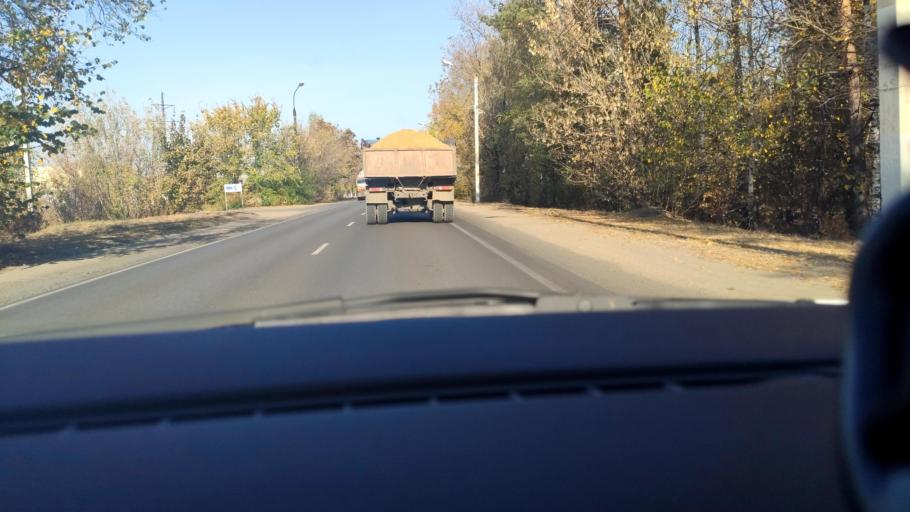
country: RU
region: Voronezj
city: Pridonskoy
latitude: 51.6347
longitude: 39.0841
